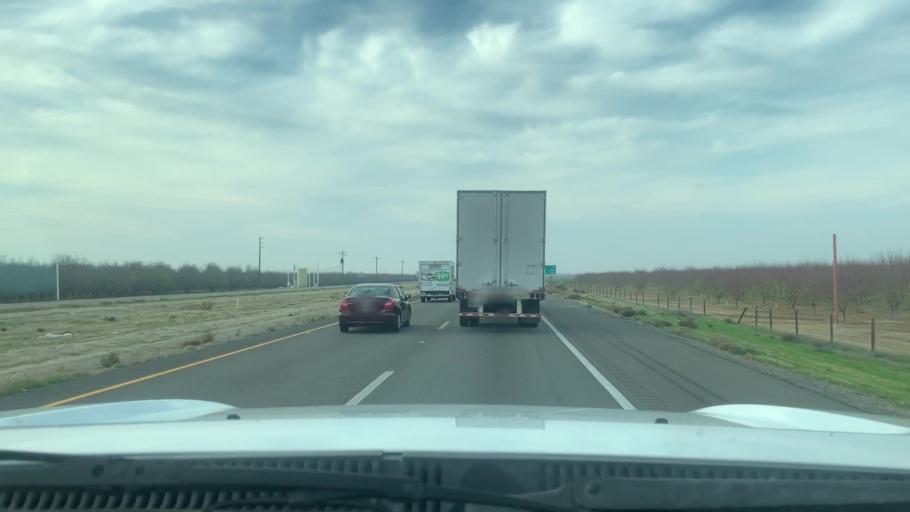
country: US
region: California
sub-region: Kern County
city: Buttonwillow
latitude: 35.4637
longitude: -119.4860
